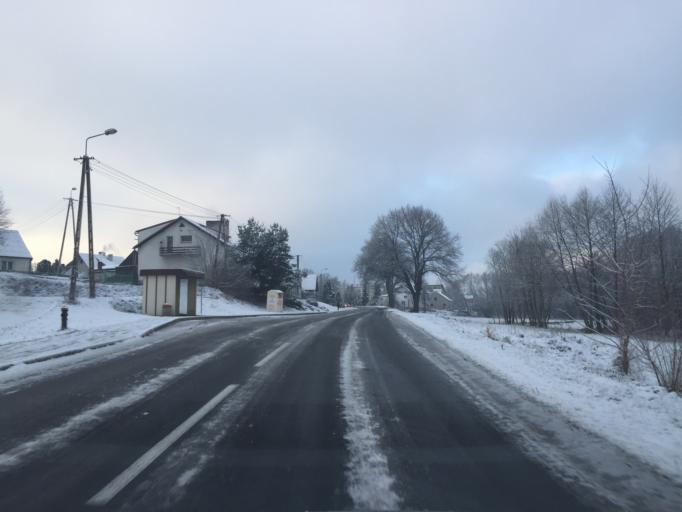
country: PL
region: Kujawsko-Pomorskie
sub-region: Powiat brodnicki
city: Bartniczka
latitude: 53.2496
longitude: 19.6059
